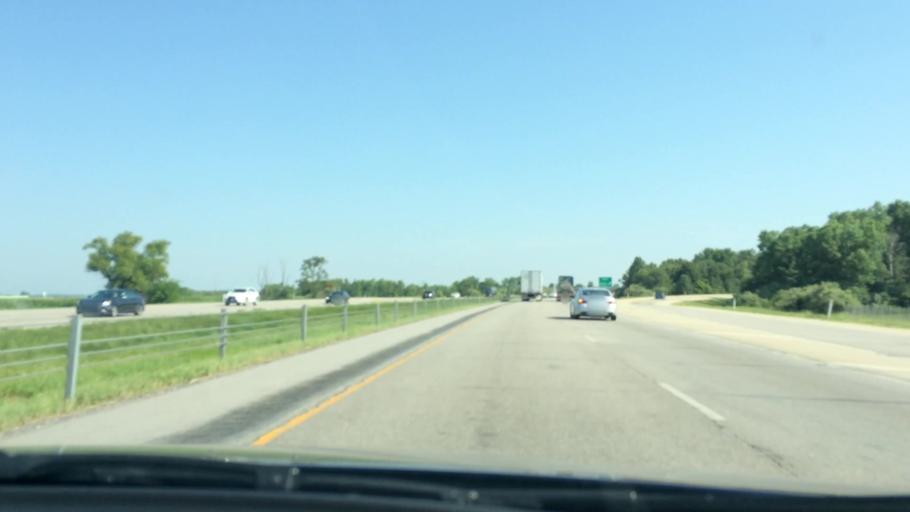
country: US
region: Indiana
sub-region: Jasper County
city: Rensselaer
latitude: 41.0069
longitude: -87.2698
